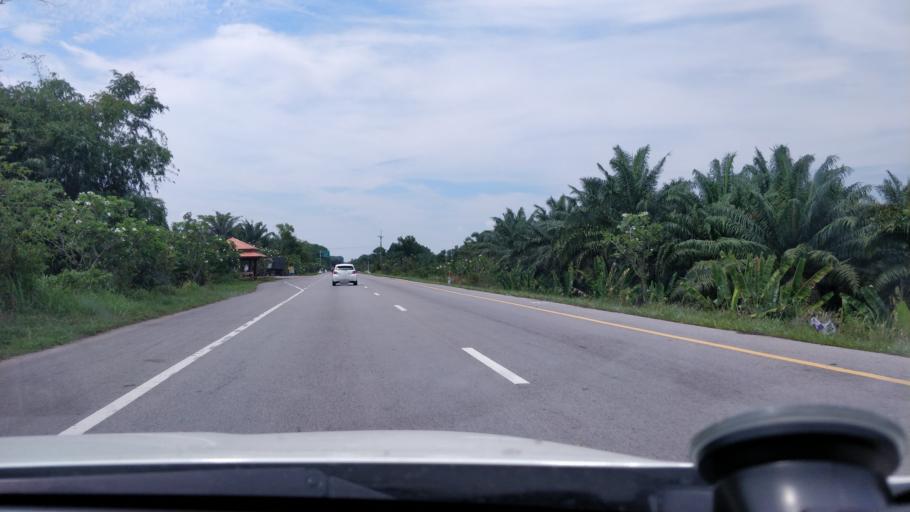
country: TH
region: Surat Thani
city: Khian Sa
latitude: 8.7832
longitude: 99.1614
